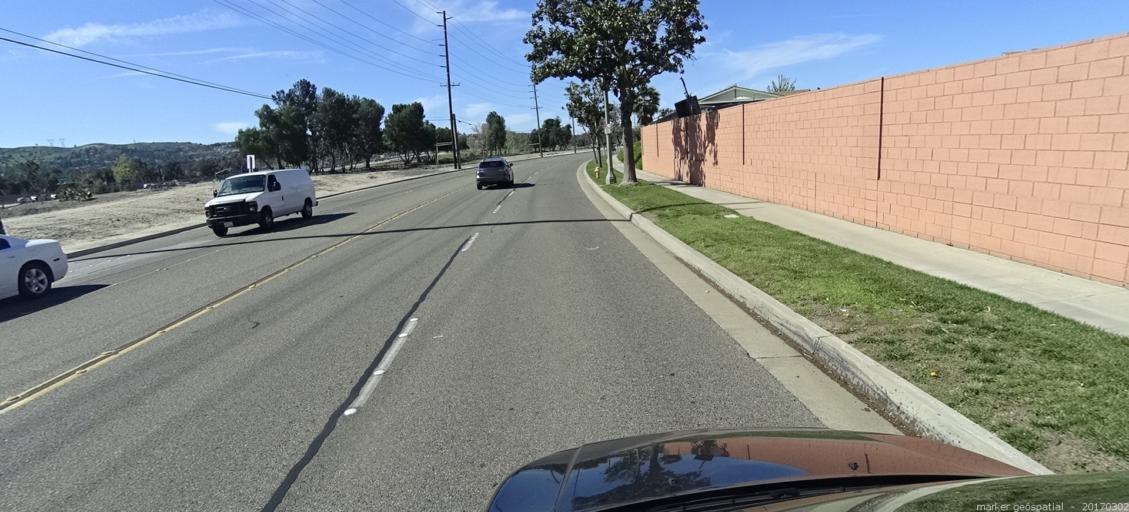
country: US
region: California
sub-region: Orange County
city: Yorba Linda
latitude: 33.8608
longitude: -117.7814
